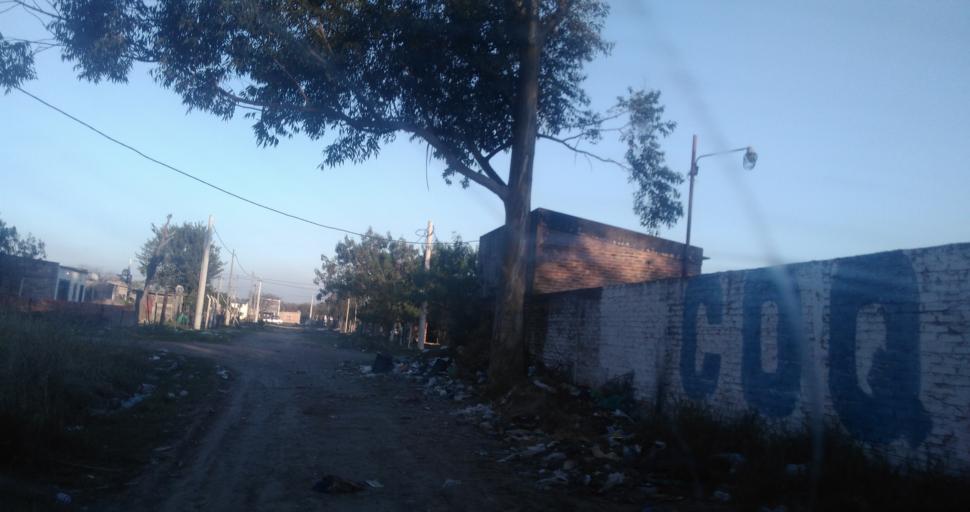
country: AR
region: Chaco
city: Fontana
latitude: -27.4614
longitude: -59.0346
